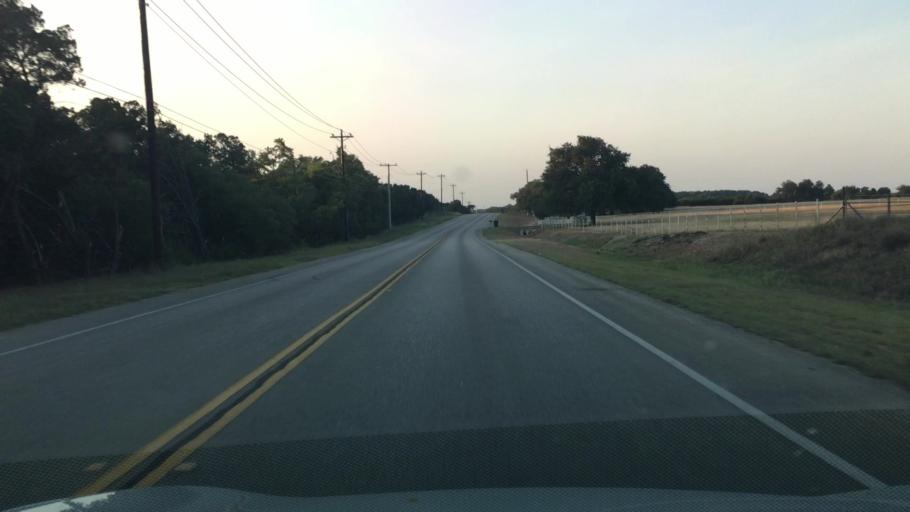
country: US
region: Texas
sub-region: Hays County
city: Dripping Springs
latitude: 30.1569
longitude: -98.0090
